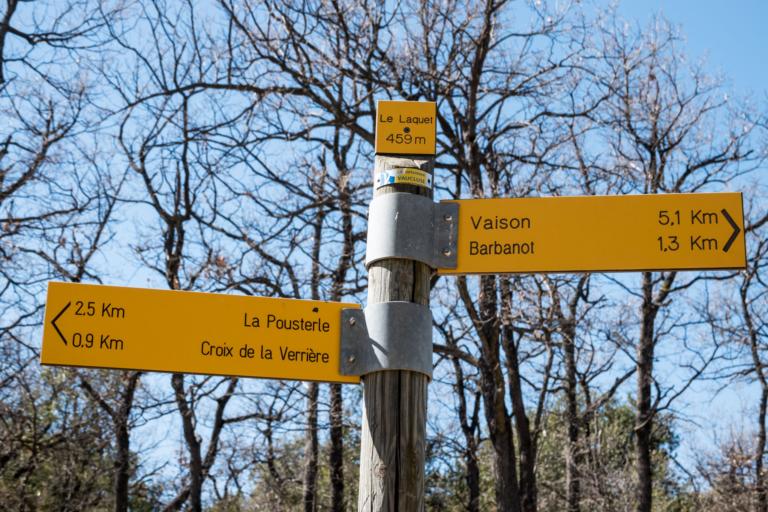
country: FR
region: Provence-Alpes-Cote d'Azur
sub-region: Departement du Vaucluse
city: Vaison-la-Romaine
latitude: 44.2047
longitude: 5.0660
